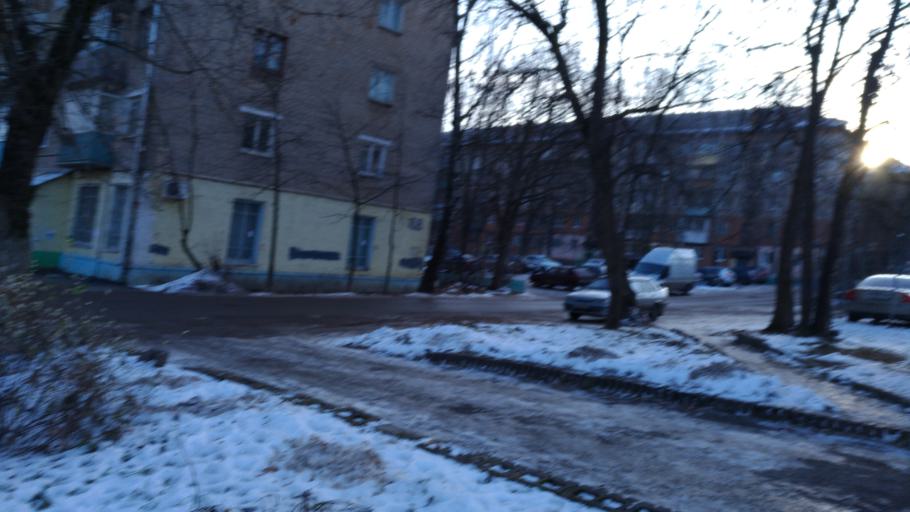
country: RU
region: Tula
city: Tula
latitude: 54.1923
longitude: 37.6947
